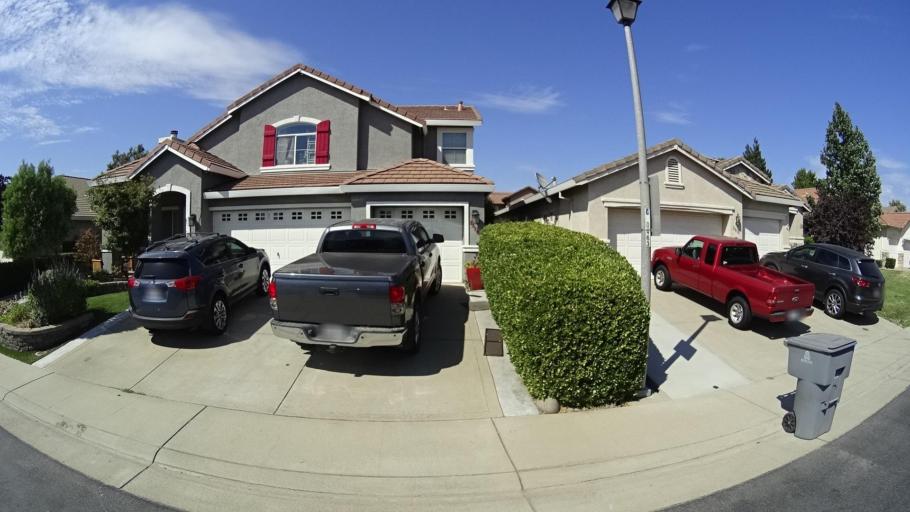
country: US
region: California
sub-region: Placer County
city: Roseville
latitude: 38.8008
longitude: -121.2865
